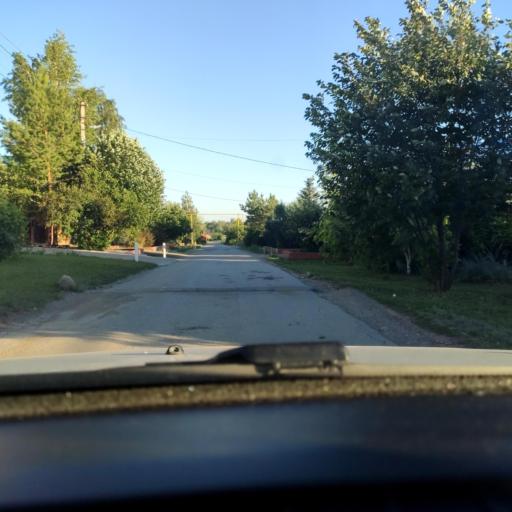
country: RU
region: Samara
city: Kinel'
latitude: 53.2707
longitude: 50.5925
